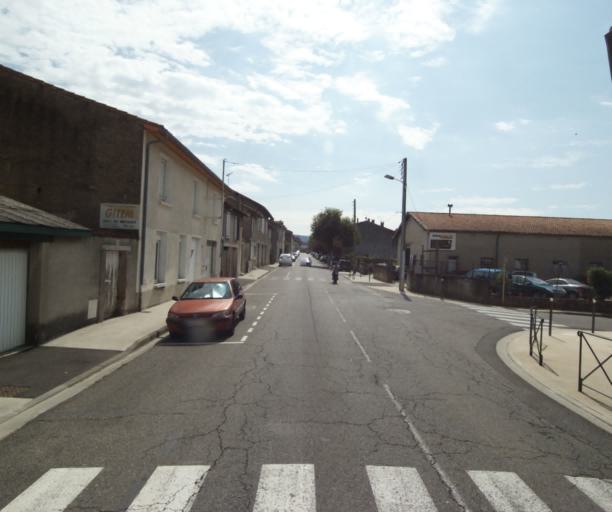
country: FR
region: Midi-Pyrenees
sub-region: Departement de la Haute-Garonne
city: Revel
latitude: 43.4608
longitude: 1.9998
